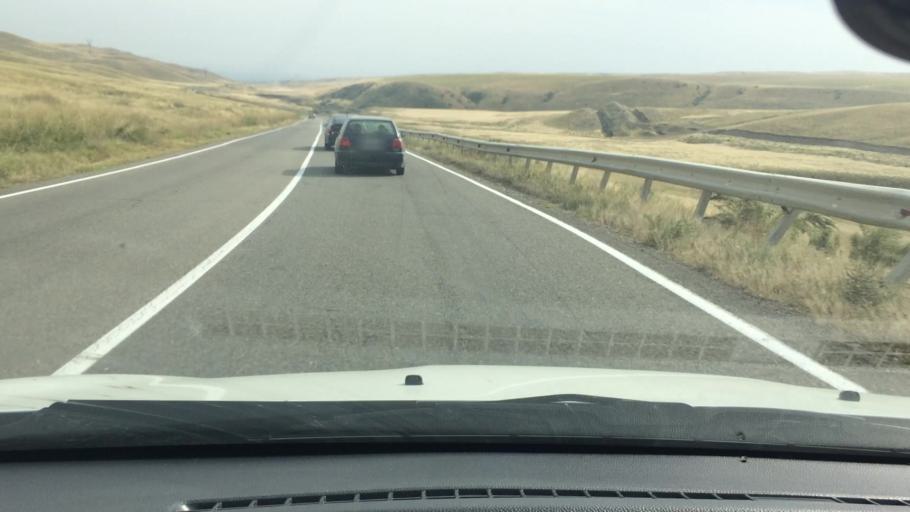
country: GE
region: Kvemo Kartli
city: Rust'avi
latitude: 41.5239
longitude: 44.9365
